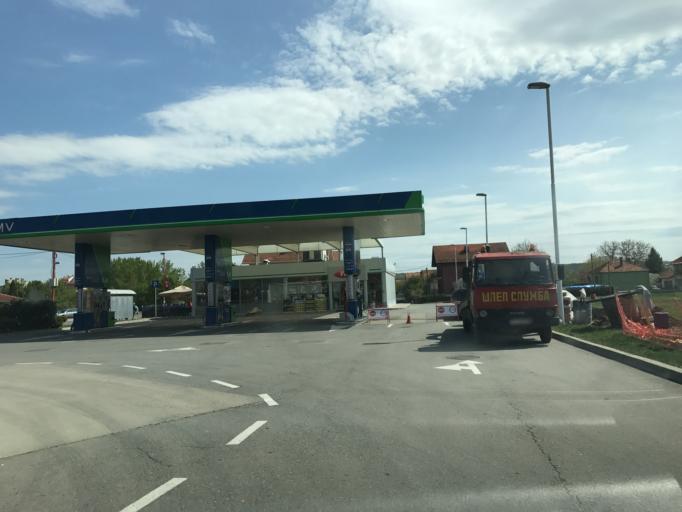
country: RS
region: Central Serbia
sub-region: Zajecarski Okrug
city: Zajecar
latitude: 43.9110
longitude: 22.2598
